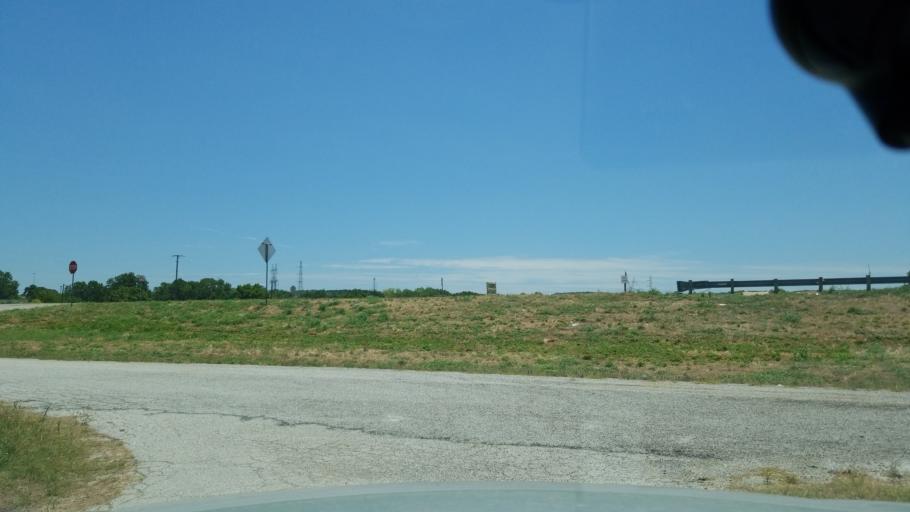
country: US
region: Texas
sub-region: Dallas County
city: Cockrell Hill
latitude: 32.7502
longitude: -96.9299
